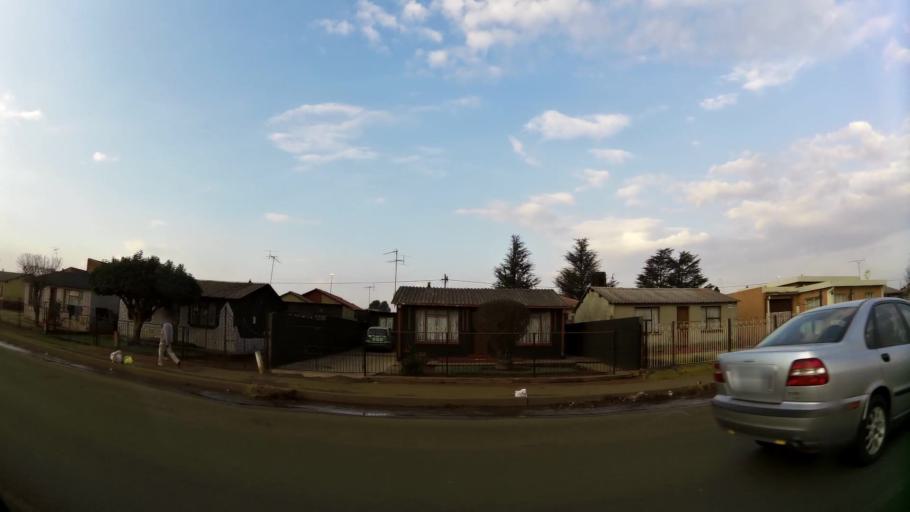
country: ZA
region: Gauteng
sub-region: City of Johannesburg Metropolitan Municipality
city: Orange Farm
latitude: -26.5745
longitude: 27.8394
